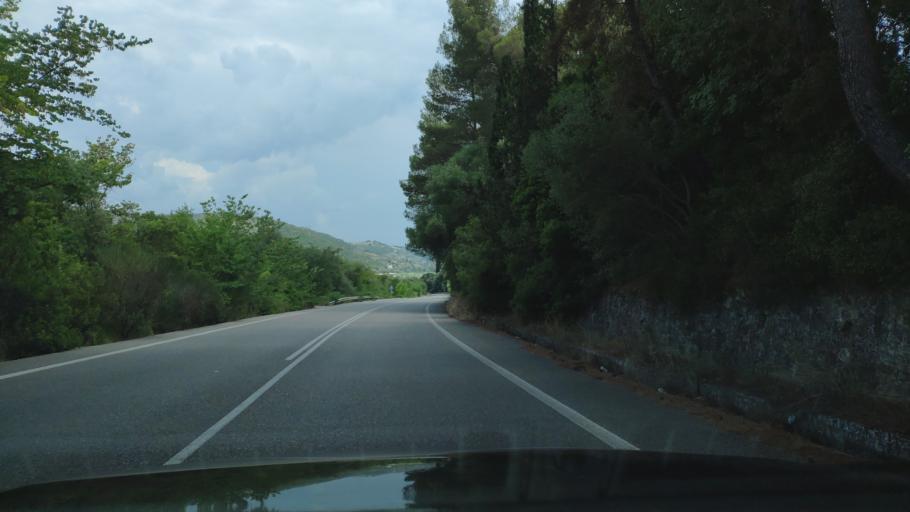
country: GR
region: West Greece
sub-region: Nomos Aitolias kai Akarnanias
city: Krikellos
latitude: 38.9931
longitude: 21.1554
